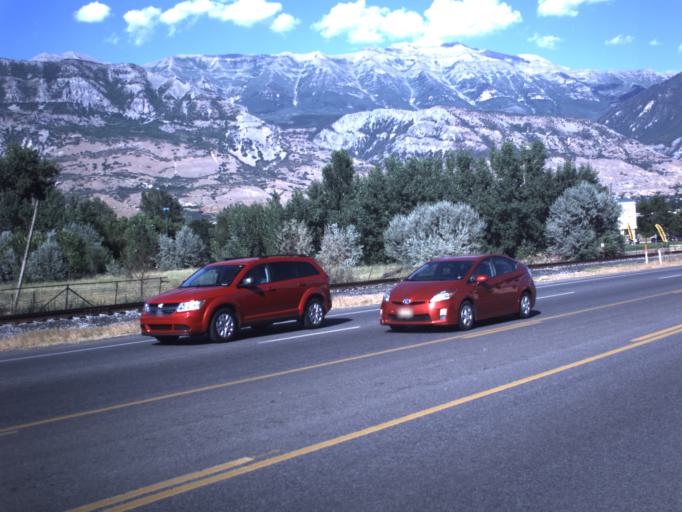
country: US
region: Utah
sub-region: Utah County
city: Pleasant Grove
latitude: 40.3671
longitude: -111.7559
